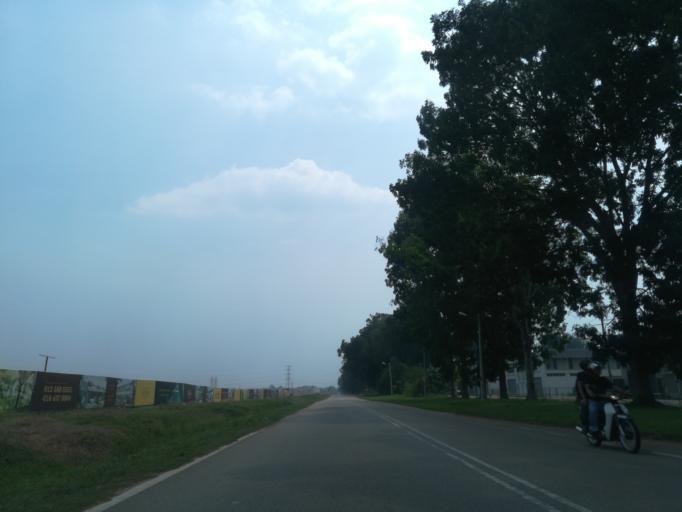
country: MY
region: Penang
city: Tasek Glugor
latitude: 5.4461
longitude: 100.5382
